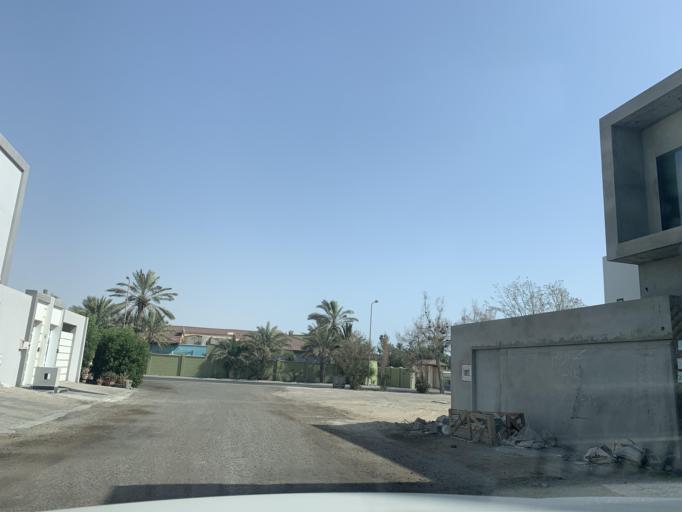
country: BH
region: Manama
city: Jidd Hafs
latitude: 26.2299
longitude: 50.4673
